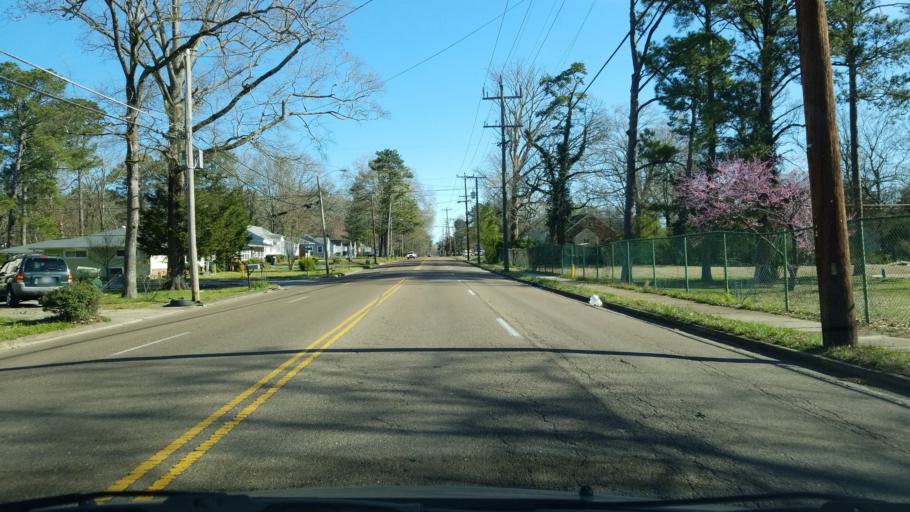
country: US
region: Tennessee
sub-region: Hamilton County
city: East Ridge
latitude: 35.0192
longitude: -85.2249
